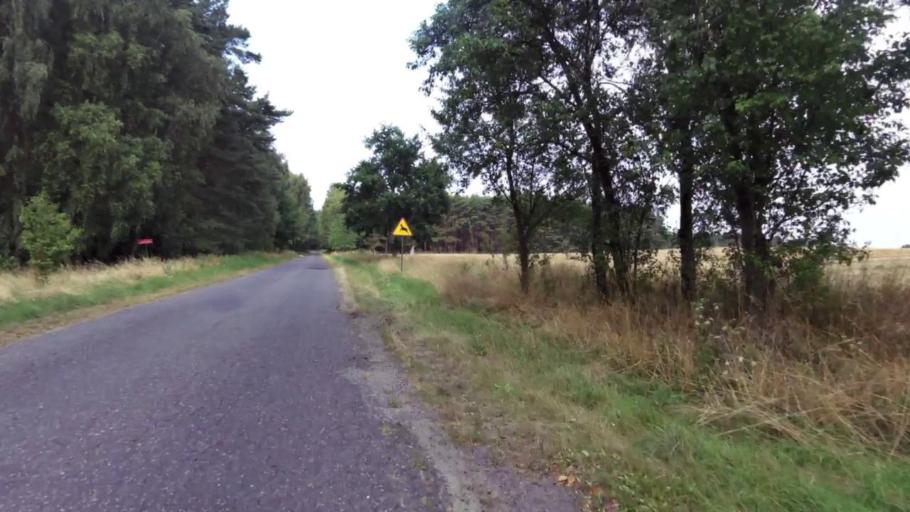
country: PL
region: West Pomeranian Voivodeship
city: Trzcinsko Zdroj
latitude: 52.8556
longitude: 14.6493
